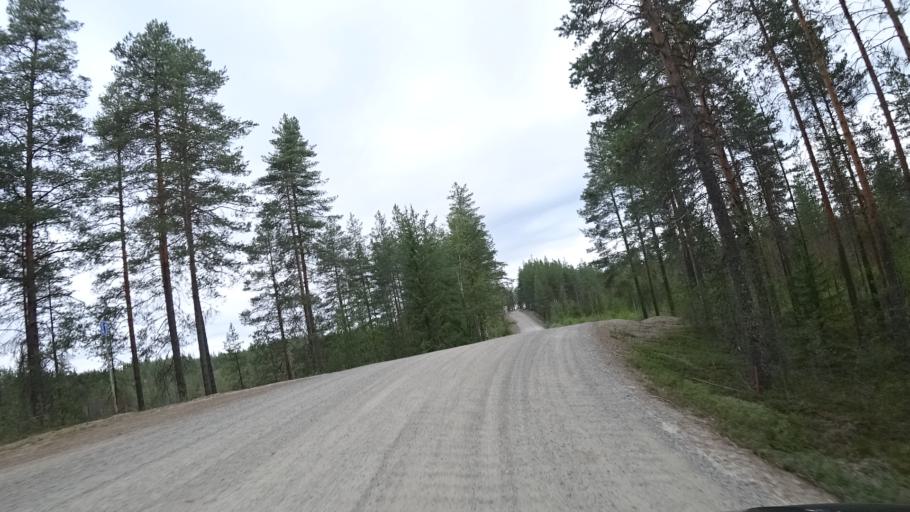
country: FI
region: North Karelia
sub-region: Pielisen Karjala
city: Lieksa
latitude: 63.2561
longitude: 30.3210
